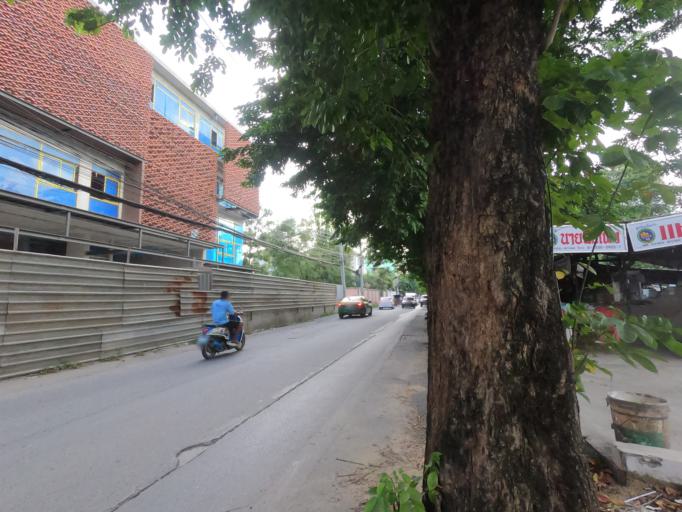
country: TH
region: Bangkok
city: Lat Phrao
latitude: 13.8209
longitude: 100.6118
